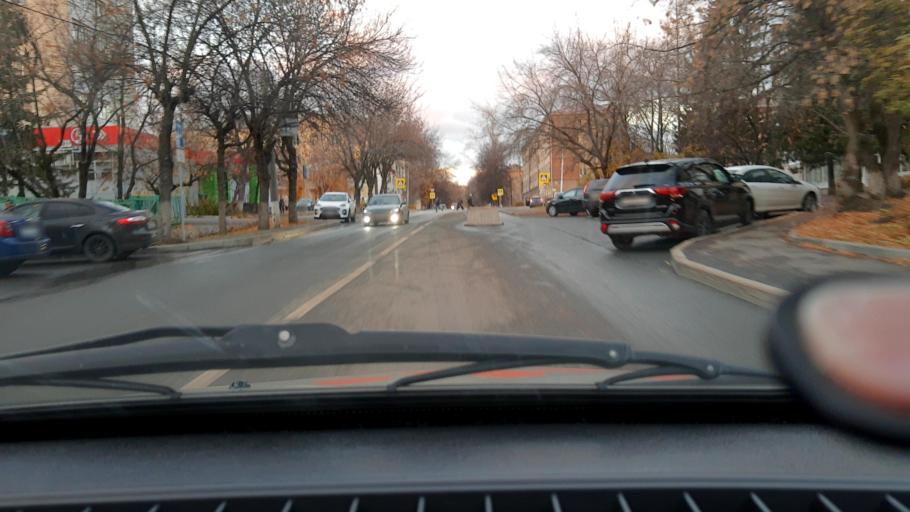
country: RU
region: Bashkortostan
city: Ufa
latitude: 54.8151
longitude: 56.0666
